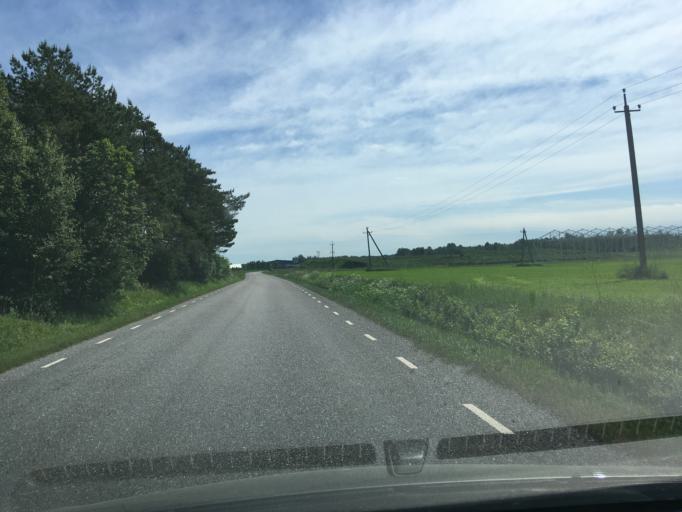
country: EE
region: Paernumaa
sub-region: Audru vald
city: Audru
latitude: 58.4284
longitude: 24.4148
